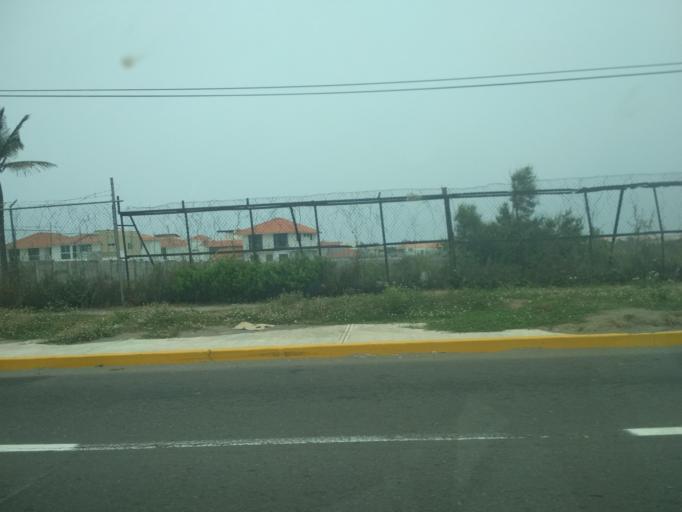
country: MX
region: Veracruz
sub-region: Alvarado
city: Playa de la Libertad
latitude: 19.0677
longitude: -96.0810
